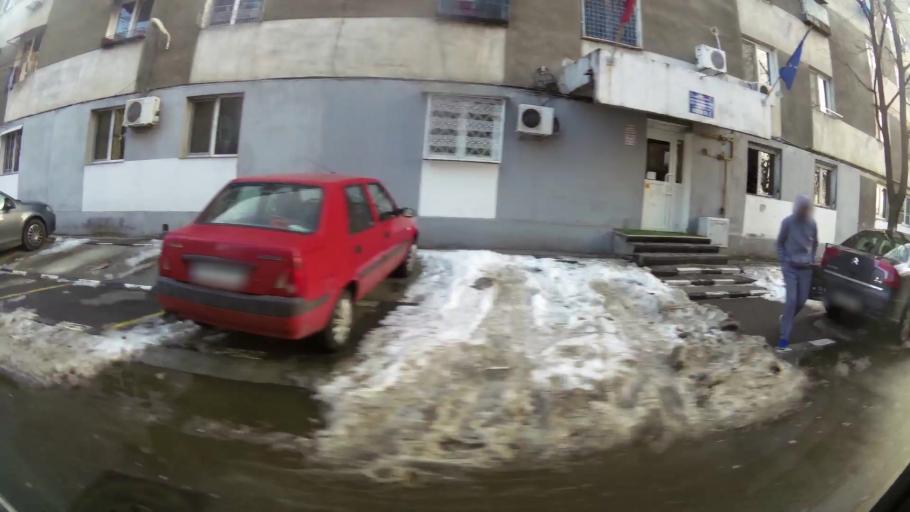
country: RO
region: Bucuresti
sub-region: Municipiul Bucuresti
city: Bucuresti
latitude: 44.3894
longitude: 26.0834
